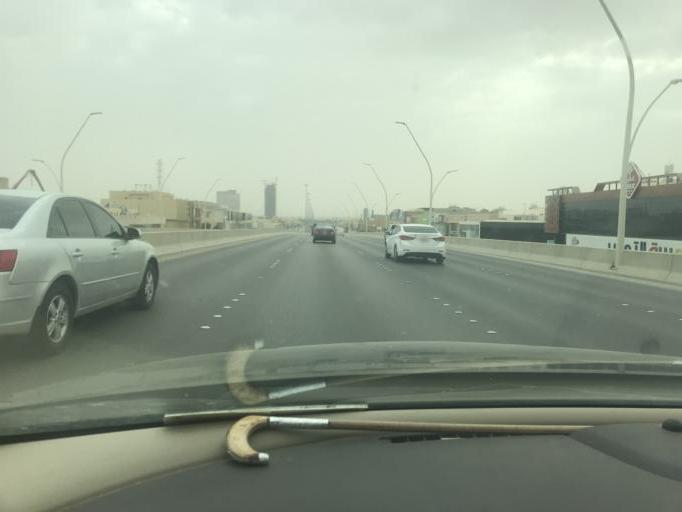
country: SA
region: Ar Riyad
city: Riyadh
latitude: 24.8187
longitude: 46.6425
